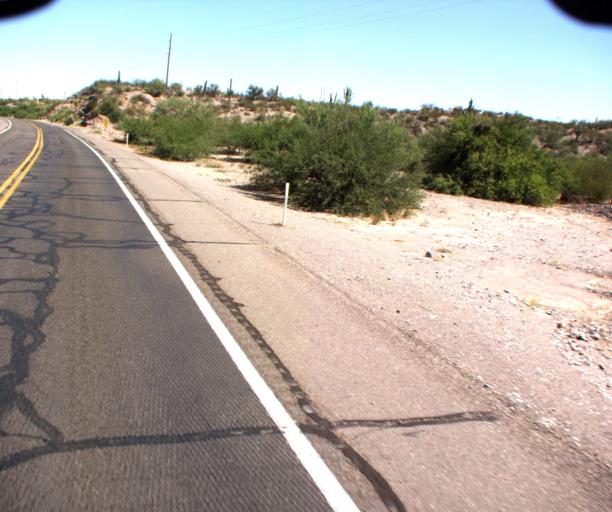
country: US
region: Arizona
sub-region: Pinal County
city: Mammoth
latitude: 32.7523
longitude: -110.6468
